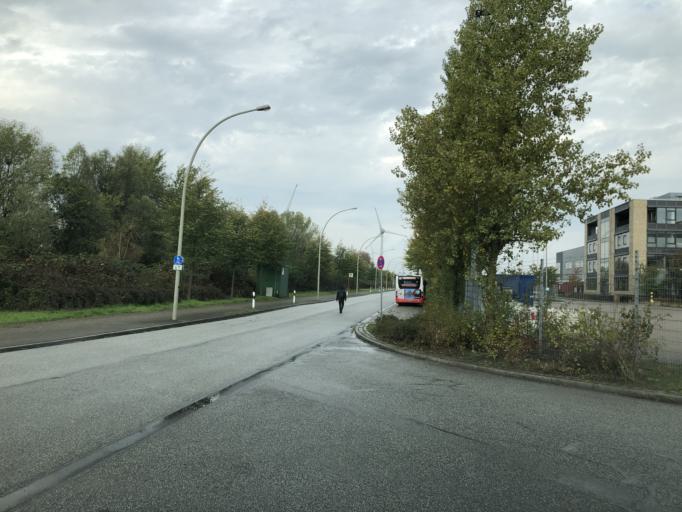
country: DE
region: Hamburg
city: Altona
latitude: 53.4980
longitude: 9.9192
